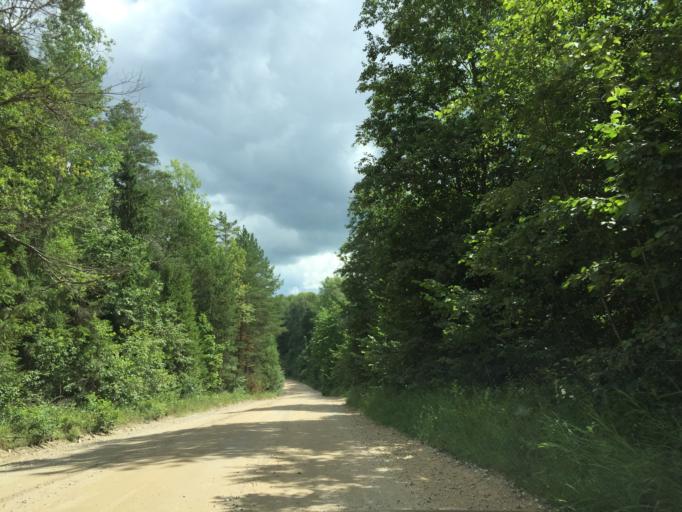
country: LV
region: Ropazu
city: Ropazi
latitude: 56.9103
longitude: 24.7639
